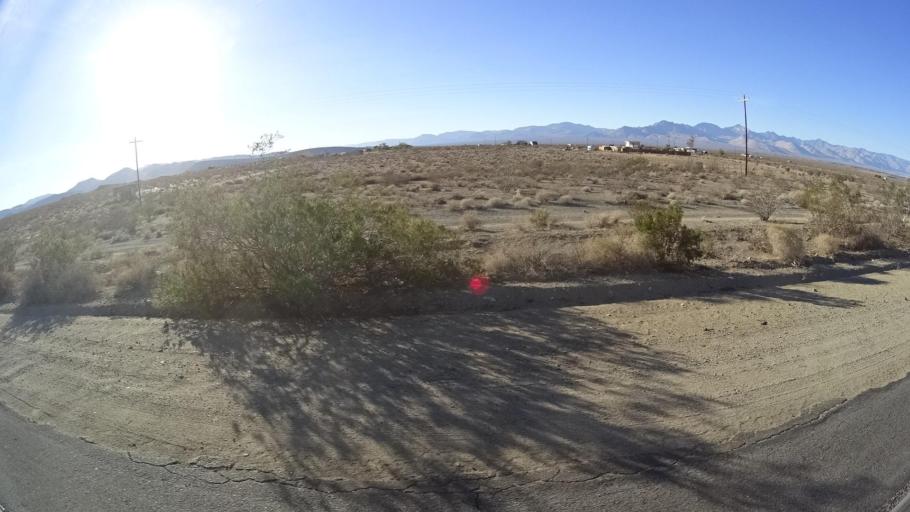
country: US
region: California
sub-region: Kern County
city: Ridgecrest
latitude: 35.5676
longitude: -117.7140
